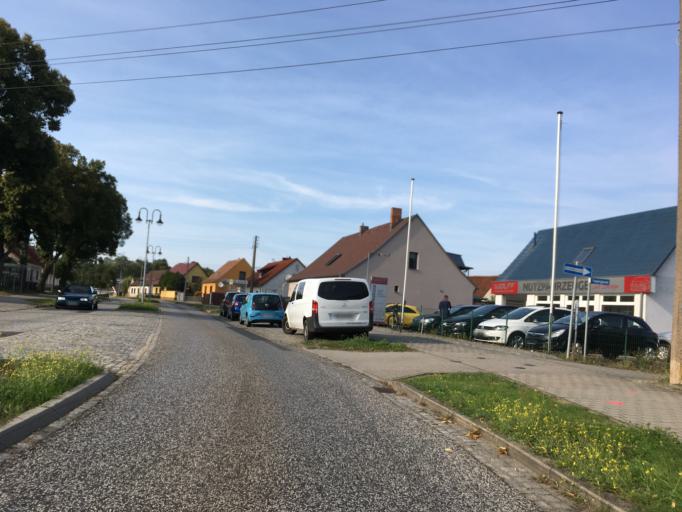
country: DE
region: Brandenburg
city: Brieskow-Finkenheerd
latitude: 52.2622
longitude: 14.5788
